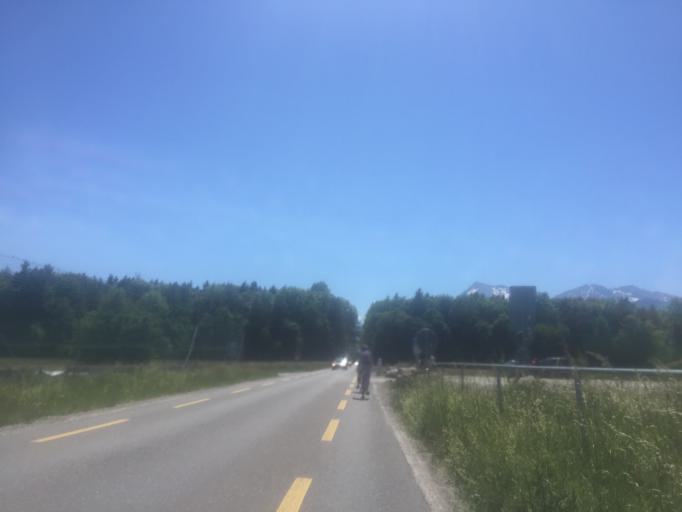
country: CH
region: Bern
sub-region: Thun District
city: Thierachern
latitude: 46.7480
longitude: 7.5910
